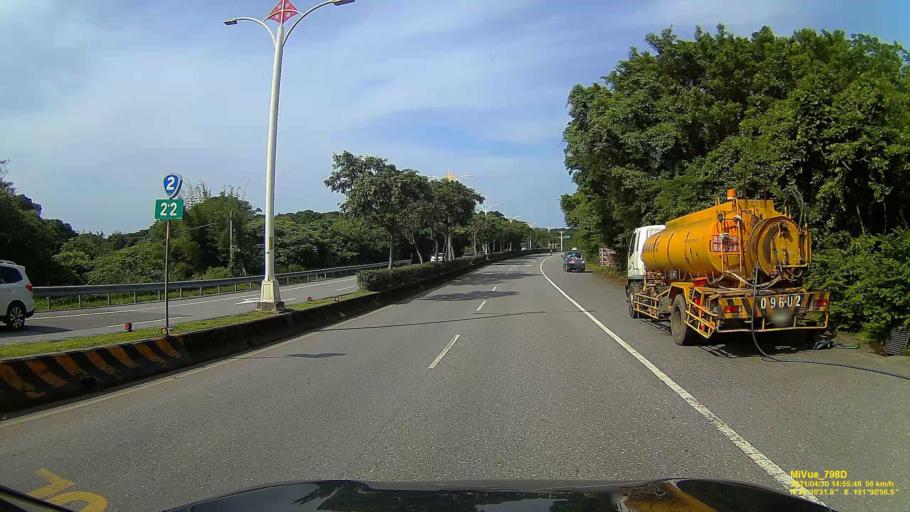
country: TW
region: Taipei
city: Taipei
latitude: 25.2757
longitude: 121.5158
